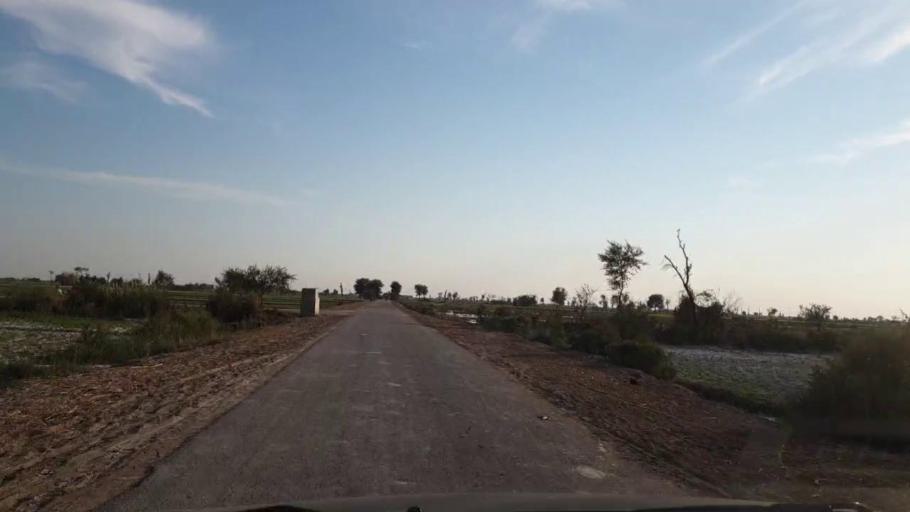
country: PK
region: Sindh
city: Khadro
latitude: 26.1649
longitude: 68.7533
